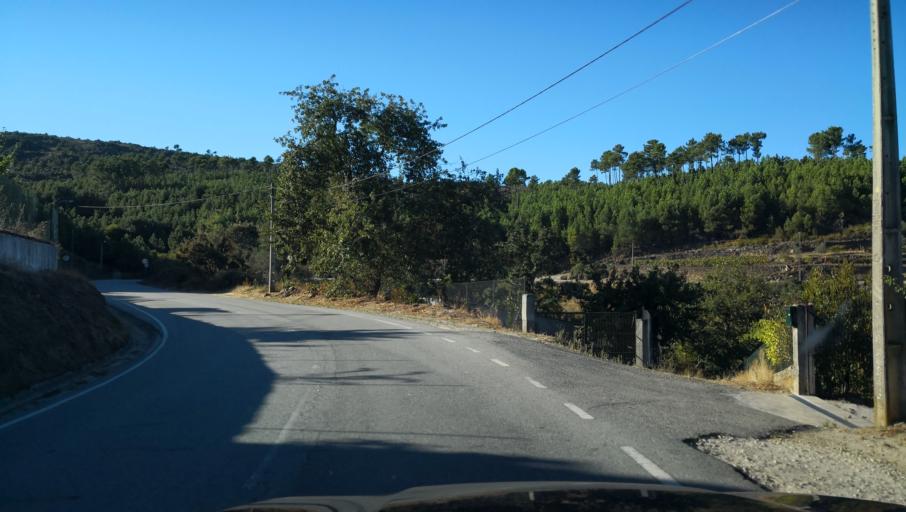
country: PT
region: Vila Real
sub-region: Sabrosa
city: Sabrosa
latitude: 41.2979
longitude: -7.5809
